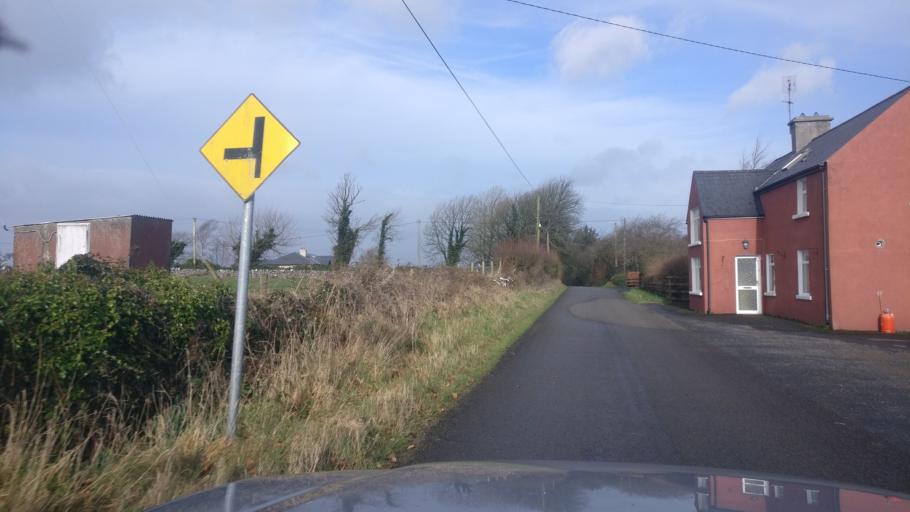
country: IE
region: Connaught
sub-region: County Galway
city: Loughrea
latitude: 53.2775
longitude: -8.5814
